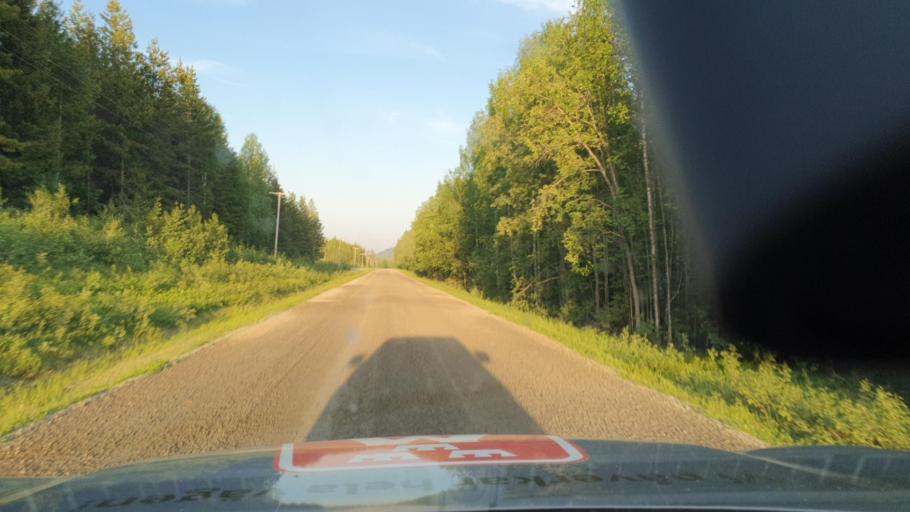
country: SE
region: Norrbotten
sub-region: Bodens Kommun
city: Boden
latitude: 66.1760
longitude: 21.5144
